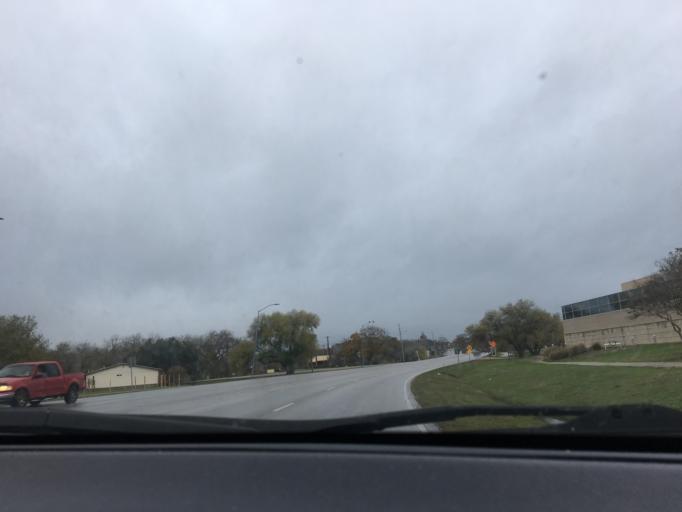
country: US
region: Texas
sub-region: Hays County
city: San Marcos
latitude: 29.8844
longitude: -97.9321
